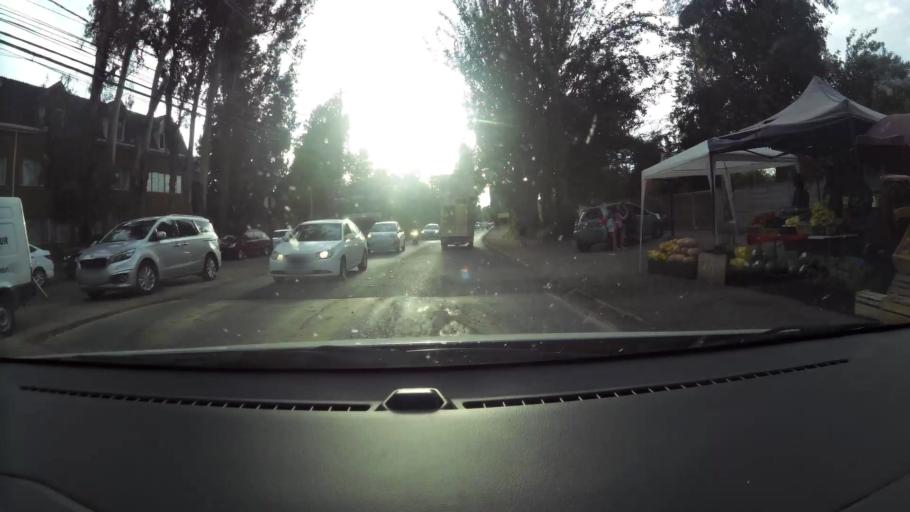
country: CL
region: Santiago Metropolitan
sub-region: Provincia de Maipo
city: San Bernardo
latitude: -33.6392
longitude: -70.6750
